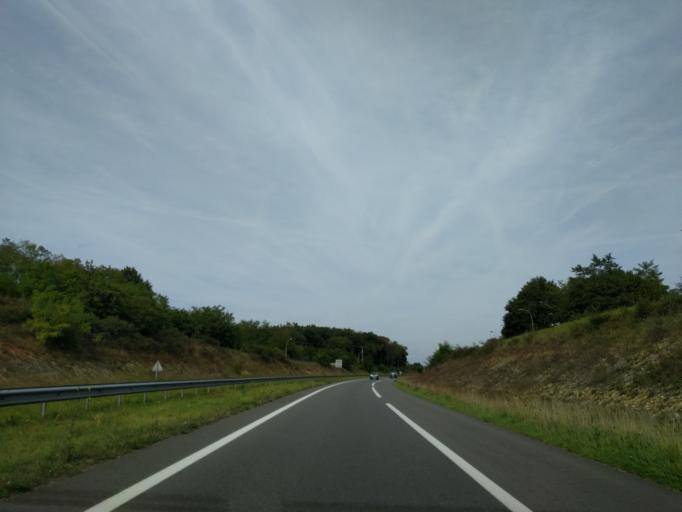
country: FR
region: Centre
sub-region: Departement du Cher
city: Bourges
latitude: 47.0626
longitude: 2.4314
